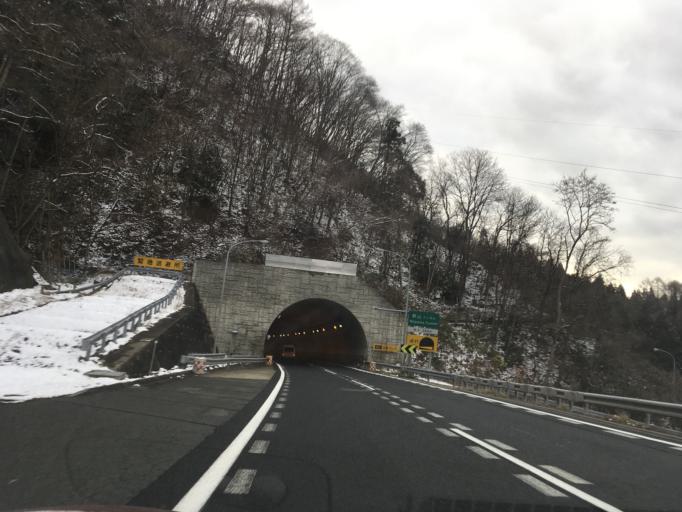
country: JP
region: Yamagata
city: Yamagata-shi
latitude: 38.2256
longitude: 140.4213
